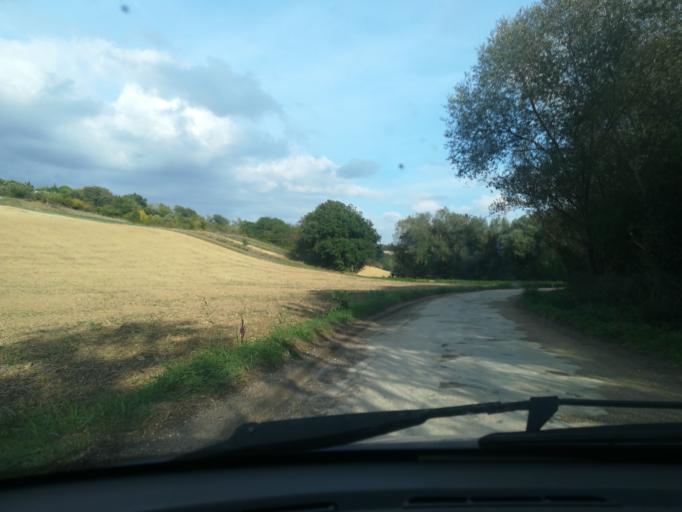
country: IT
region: The Marches
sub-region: Provincia di Macerata
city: Macerata
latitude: 43.3159
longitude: 13.4614
